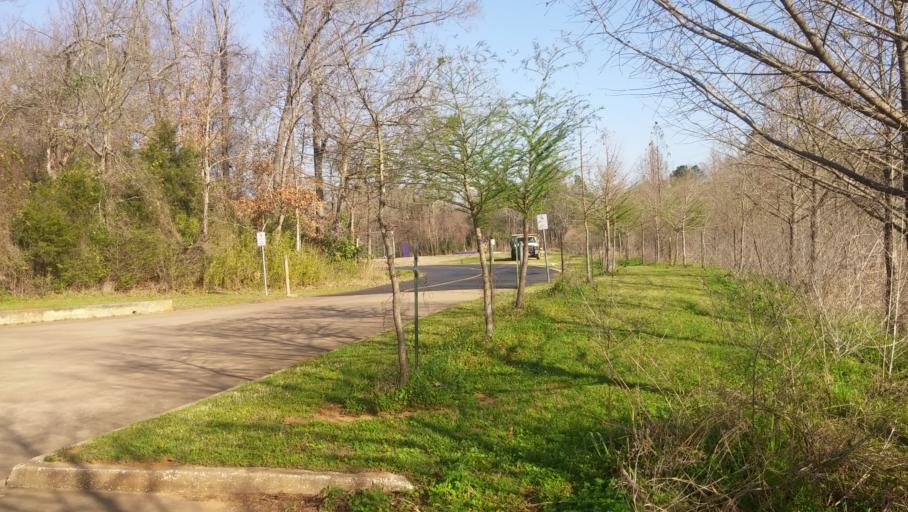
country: US
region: Texas
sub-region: Nacogdoches County
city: Nacogdoches
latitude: 31.6257
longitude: -94.6422
